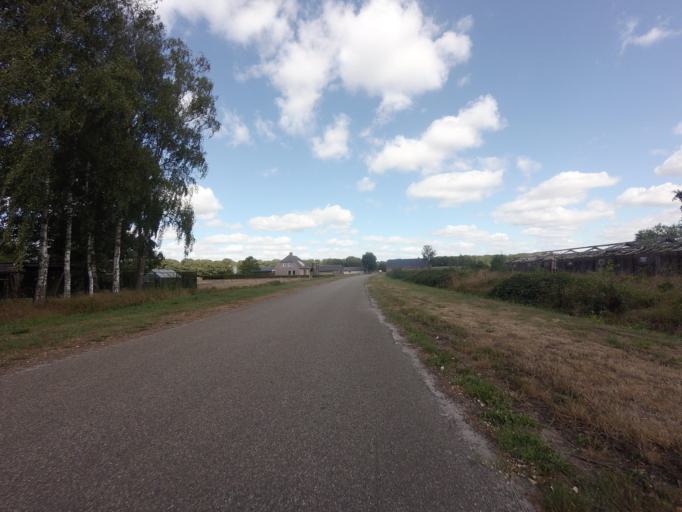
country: NL
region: North Brabant
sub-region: Gemeente Landerd
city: Schaijk
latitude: 51.7494
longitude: 5.6082
